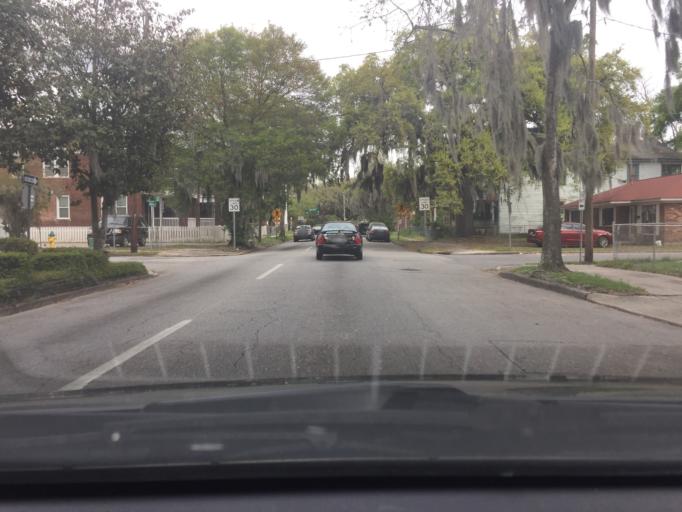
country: US
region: Georgia
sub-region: Chatham County
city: Savannah
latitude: 32.0584
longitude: -81.0833
